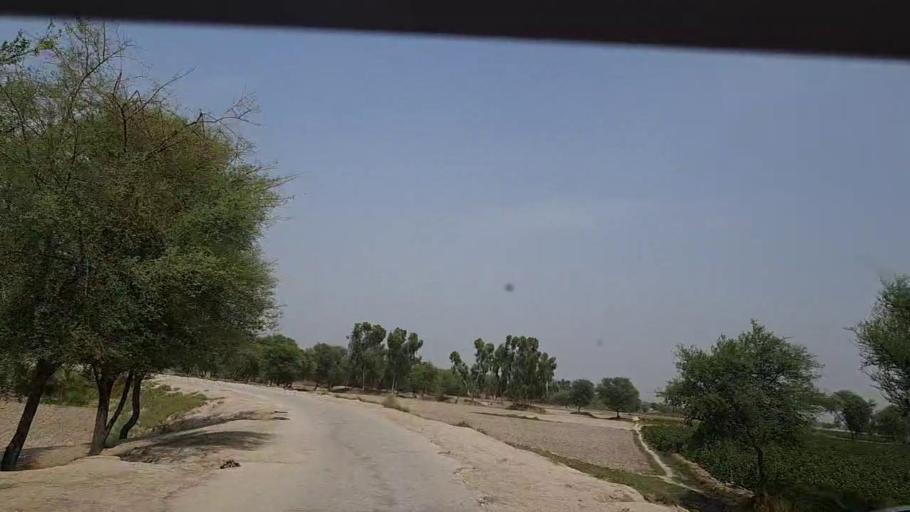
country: PK
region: Sindh
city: Khairpur Nathan Shah
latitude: 27.0810
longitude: 67.6607
